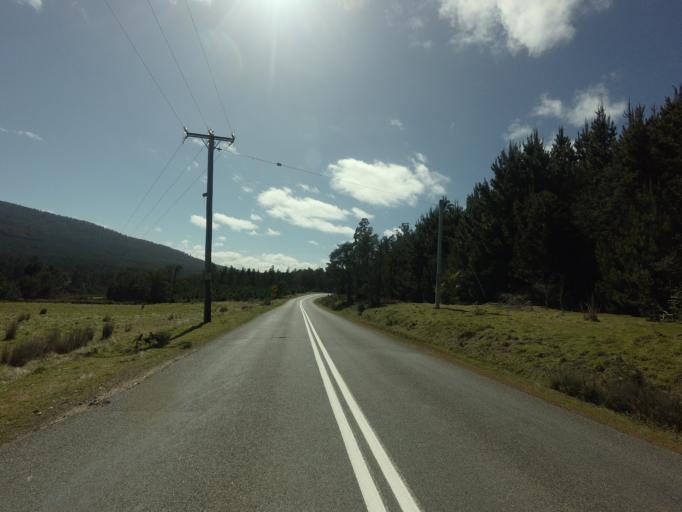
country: AU
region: Tasmania
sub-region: Derwent Valley
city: New Norfolk
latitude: -42.7416
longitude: 146.6580
